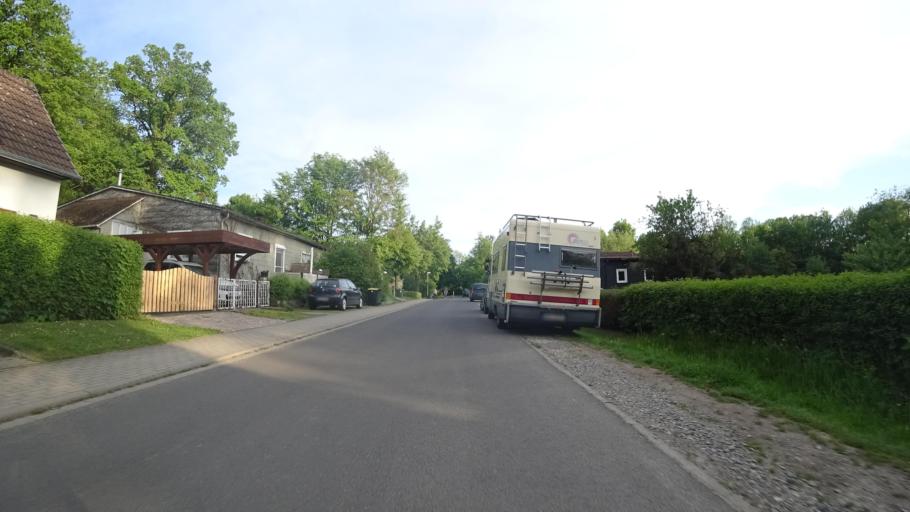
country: DE
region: Hesse
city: Grebenstein
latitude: 51.4415
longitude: 9.4118
